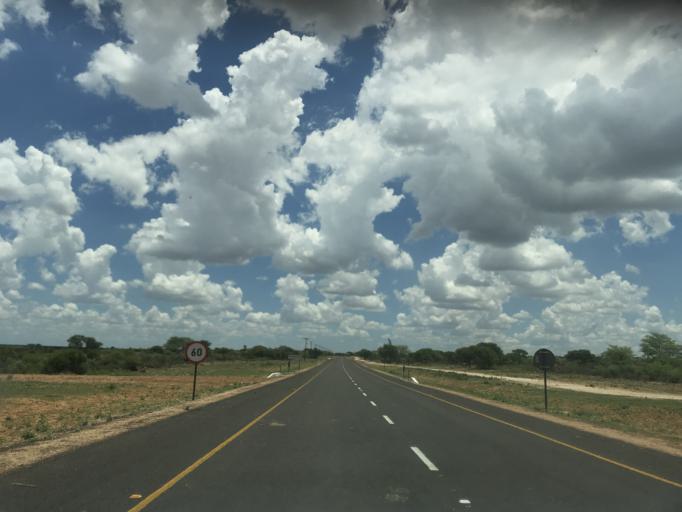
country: BW
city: Mabuli
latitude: -25.8037
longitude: 24.8283
